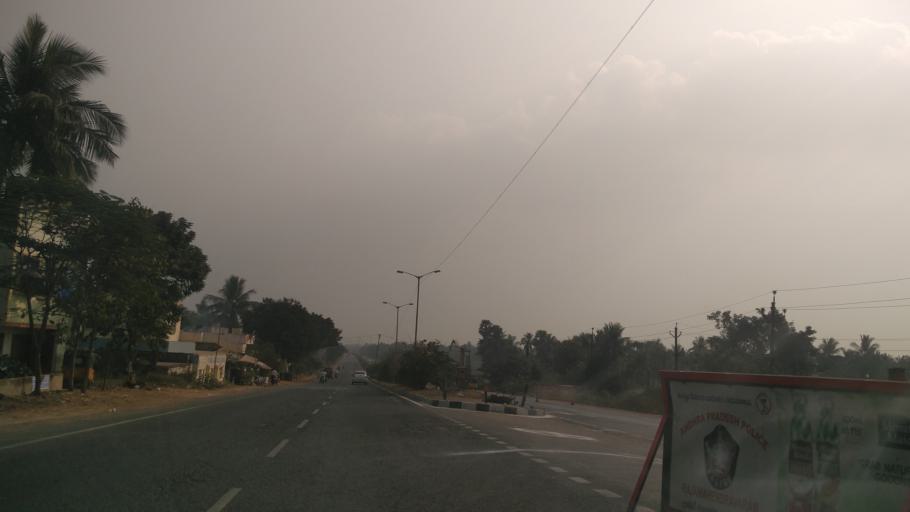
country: IN
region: Andhra Pradesh
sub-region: East Godavari
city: Rajahmundry
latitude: 16.9546
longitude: 81.7929
